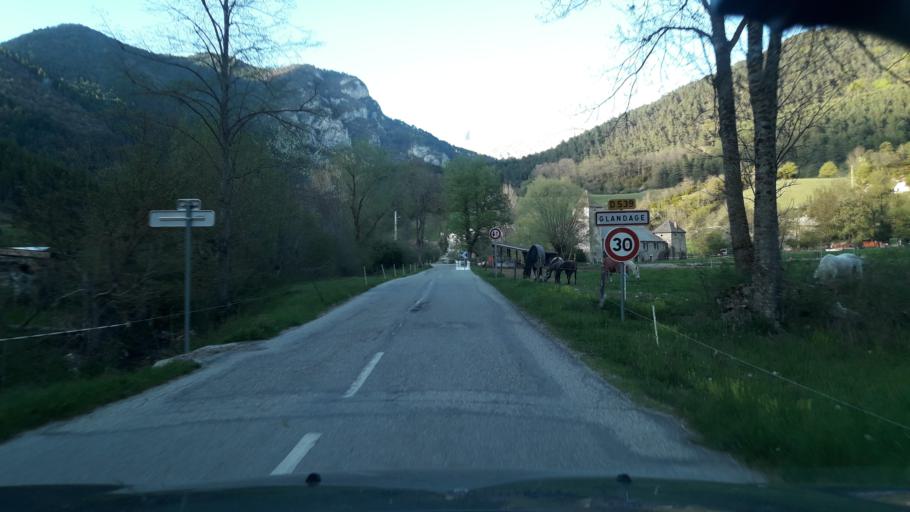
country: FR
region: Rhone-Alpes
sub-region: Departement de l'Isere
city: Mens
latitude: 44.6849
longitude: 5.5949
